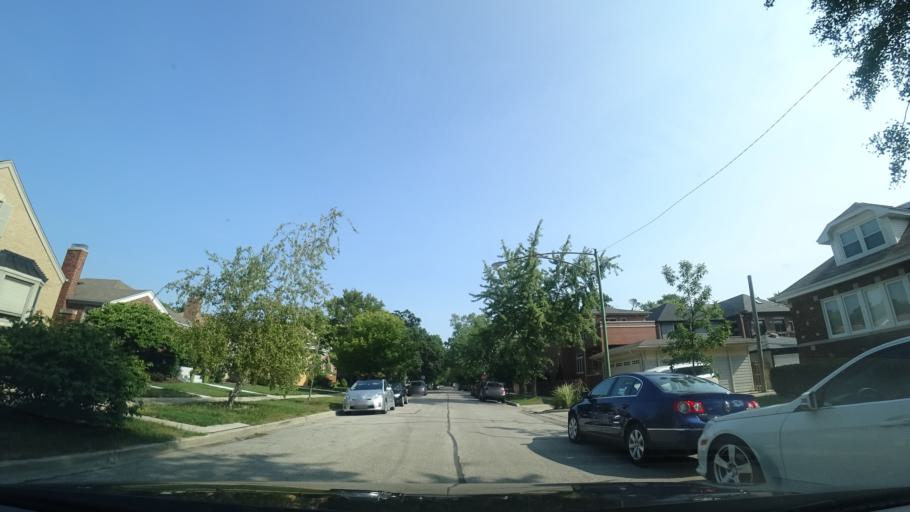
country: US
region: Illinois
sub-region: Cook County
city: Lincolnwood
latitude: 41.9839
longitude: -87.7384
